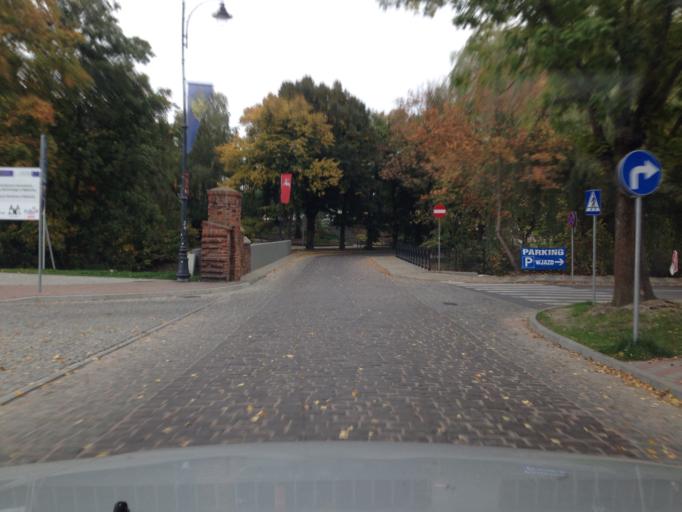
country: PL
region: Pomeranian Voivodeship
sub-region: Powiat malborski
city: Malbork
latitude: 54.0387
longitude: 19.0299
